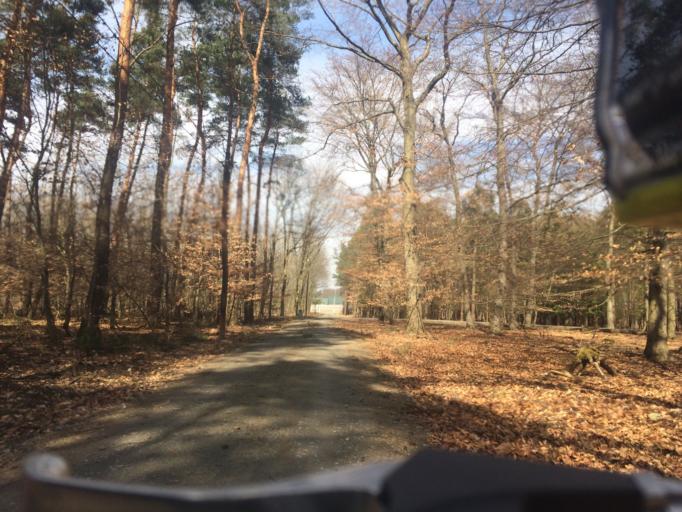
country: DE
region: Hesse
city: Kelsterbach
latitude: 50.0338
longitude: 8.5021
